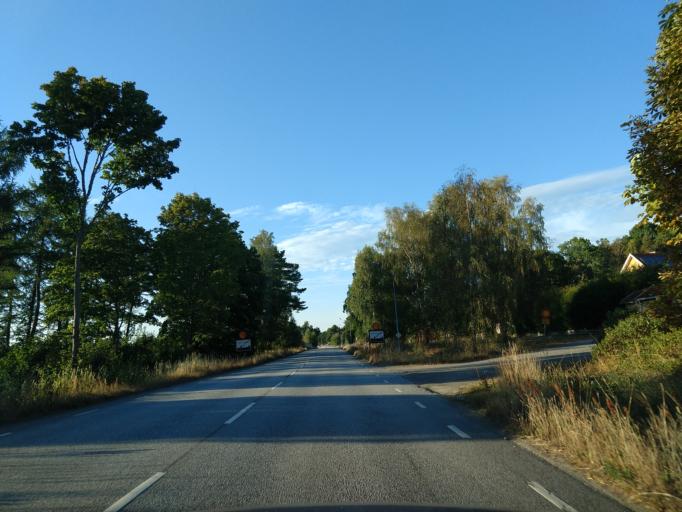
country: SE
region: Blekinge
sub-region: Ronneby Kommun
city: Brakne-Hoby
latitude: 56.2390
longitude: 15.1170
